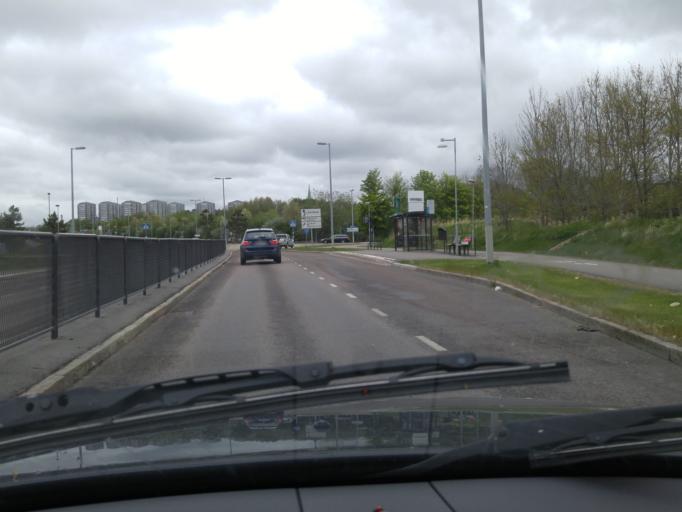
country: SE
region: Vaestra Goetaland
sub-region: Goteborg
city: Majorna
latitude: 57.6430
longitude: 11.9168
